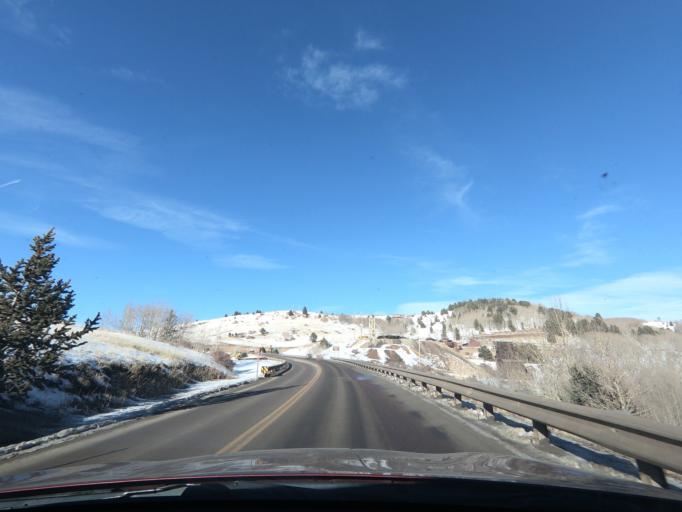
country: US
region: Colorado
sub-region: Teller County
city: Cripple Creek
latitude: 38.7517
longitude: -105.1616
